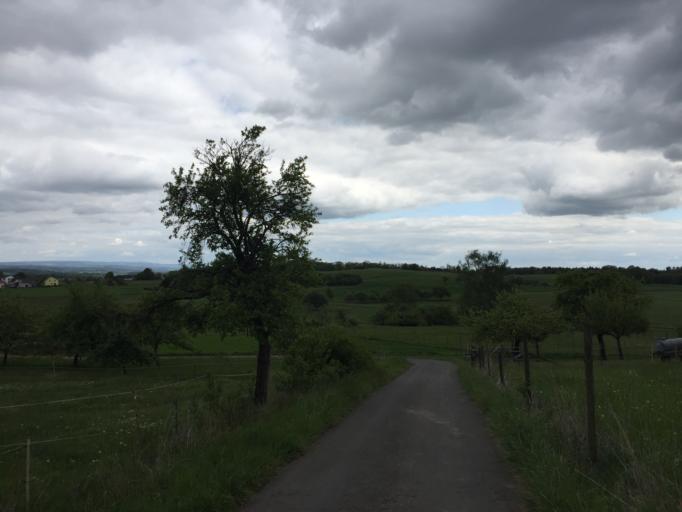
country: DE
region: Hesse
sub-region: Regierungsbezirk Giessen
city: Reiskirchen
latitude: 50.5731
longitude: 8.8429
